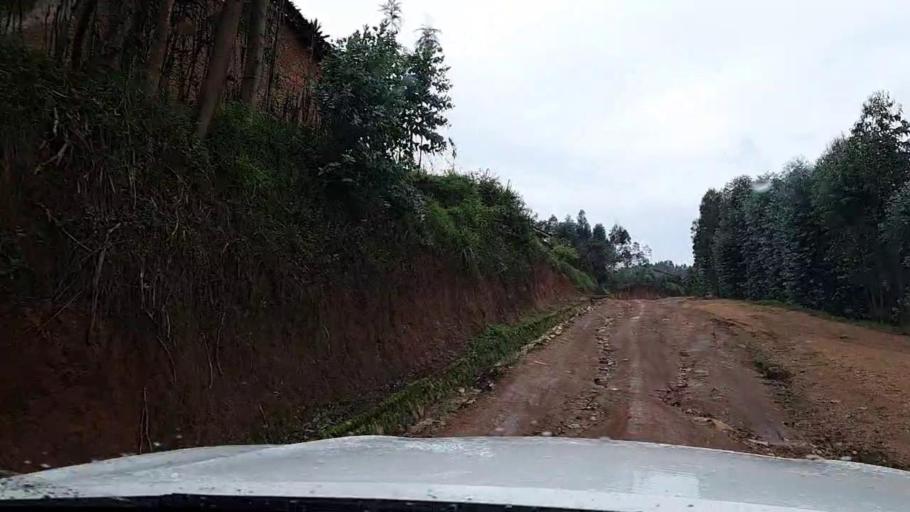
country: RW
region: Southern Province
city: Nzega
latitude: -2.4675
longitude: 29.5034
